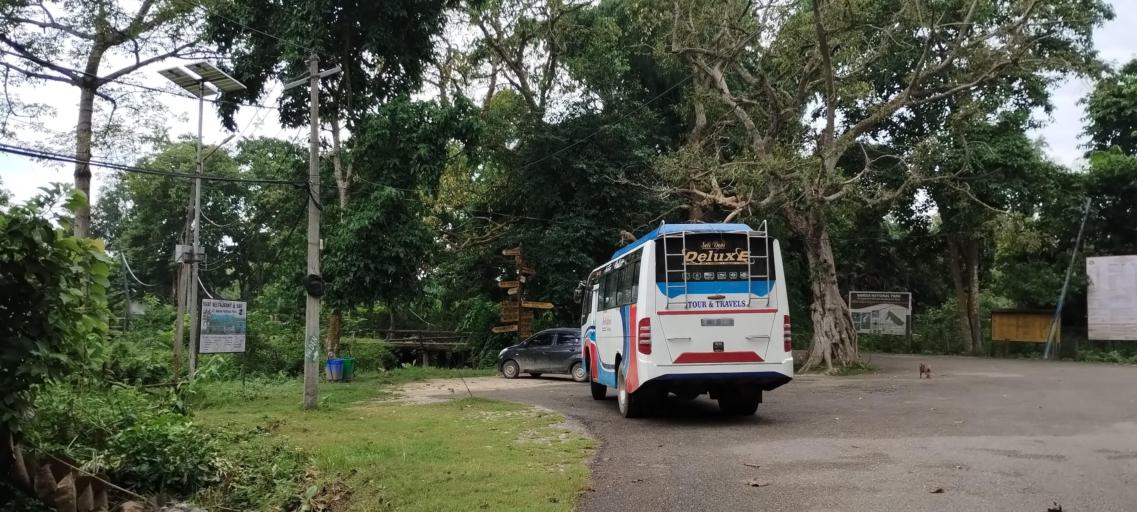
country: NP
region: Far Western
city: Tikapur
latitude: 28.4522
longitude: 81.2434
